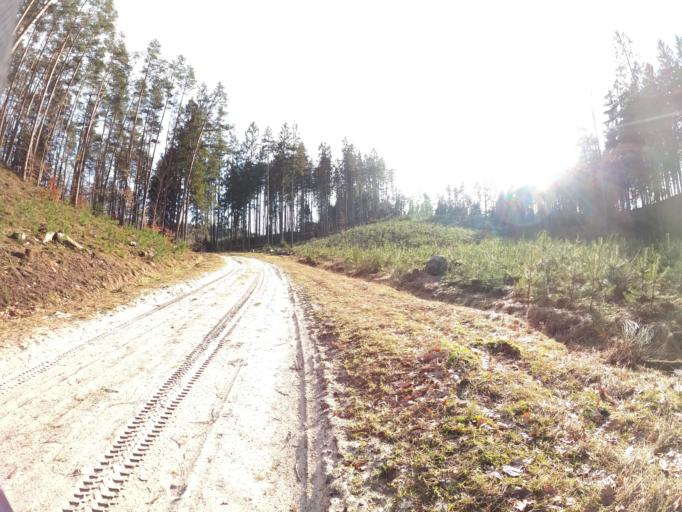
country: PL
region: West Pomeranian Voivodeship
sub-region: Powiat koszalinski
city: Polanow
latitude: 54.2176
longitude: 16.6411
